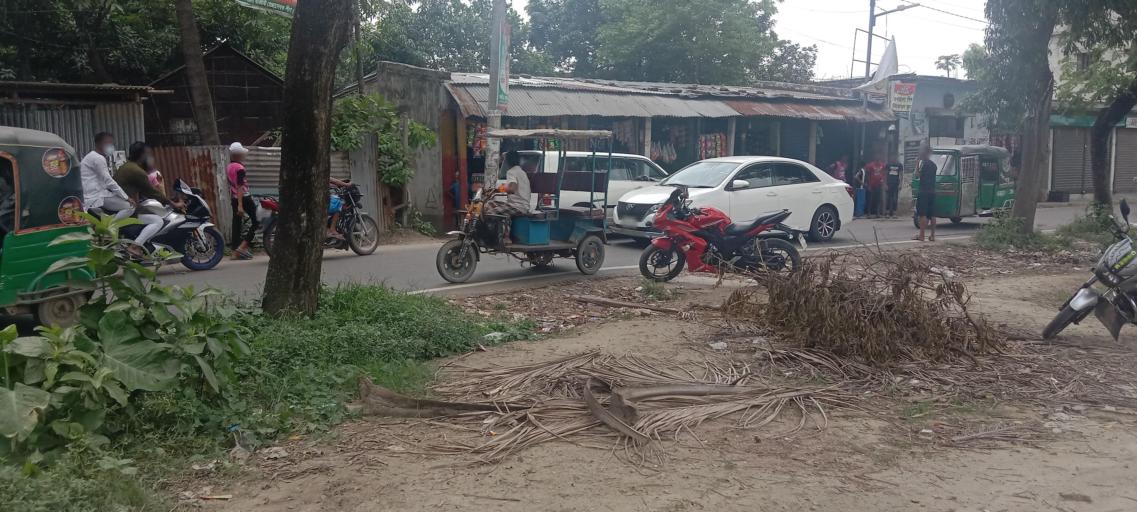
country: BD
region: Dhaka
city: Azimpur
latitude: 23.7113
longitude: 90.3459
